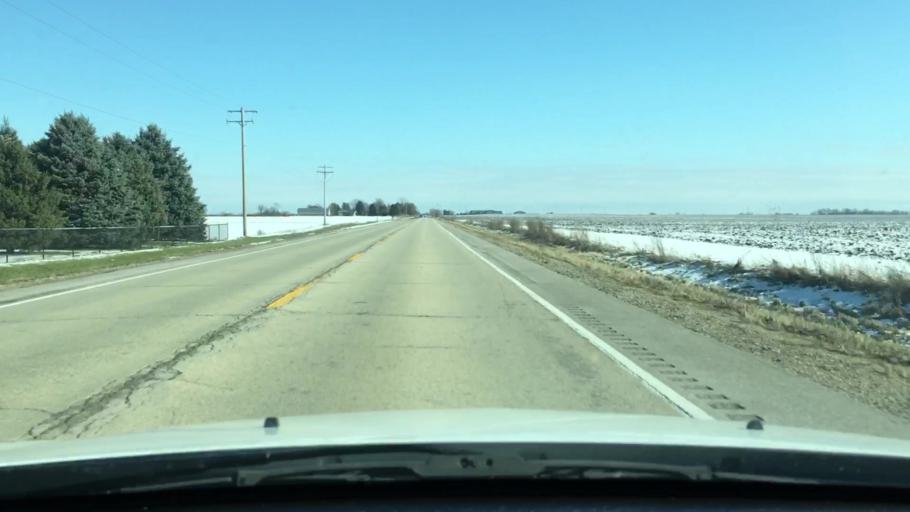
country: US
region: Illinois
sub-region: DeKalb County
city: DeKalb
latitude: 42.0015
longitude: -88.8004
